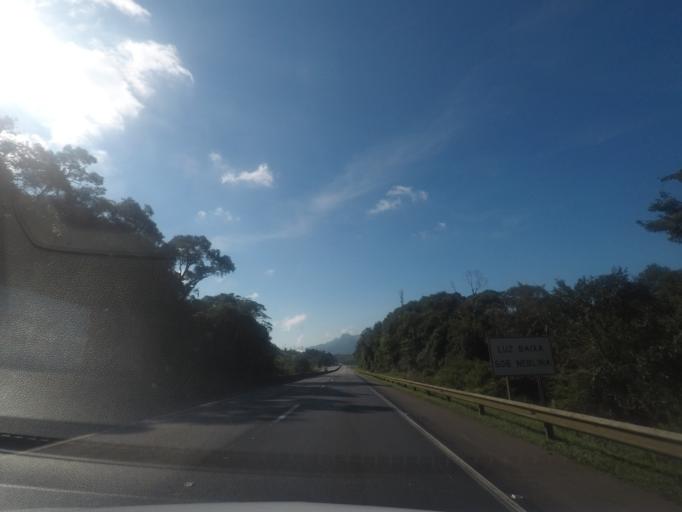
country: BR
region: Parana
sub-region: Piraquara
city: Piraquara
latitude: -25.5861
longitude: -48.9550
